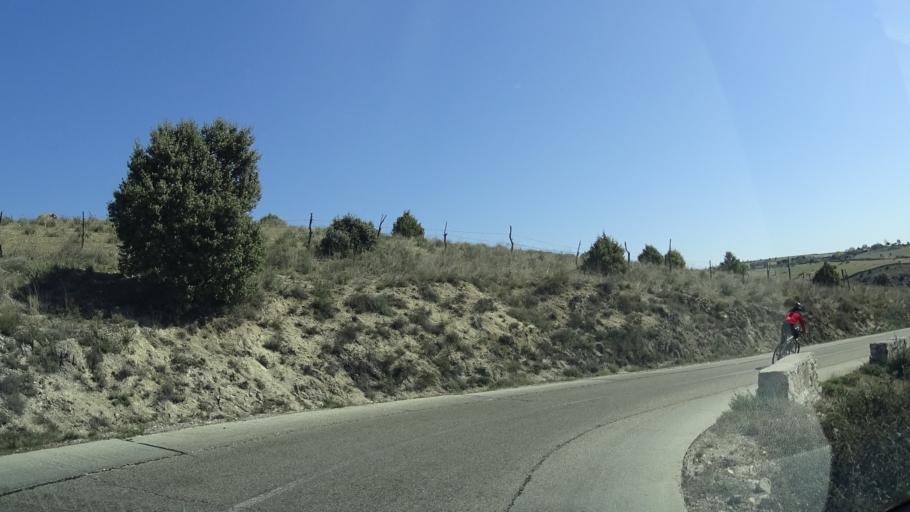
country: ES
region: Madrid
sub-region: Provincia de Madrid
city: Colmenar Viejo
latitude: 40.6457
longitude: -3.8106
